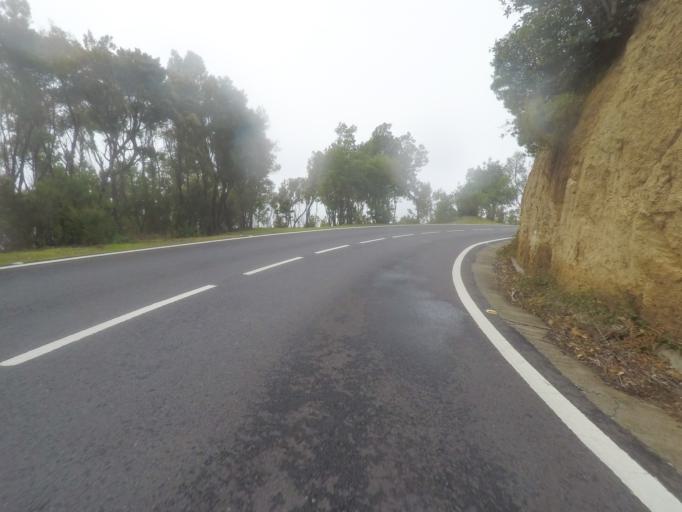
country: ES
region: Canary Islands
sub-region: Provincia de Santa Cruz de Tenerife
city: Alajero
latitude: 28.1205
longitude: -17.2496
